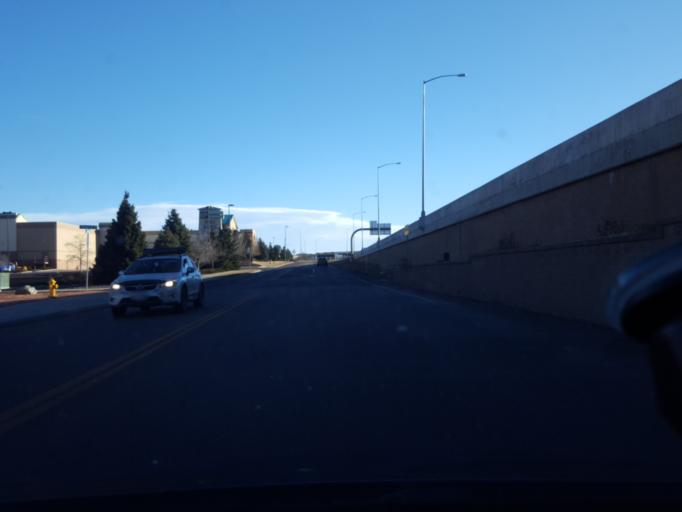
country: US
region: Colorado
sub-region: Adams County
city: Aurora
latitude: 39.7171
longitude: -104.8263
